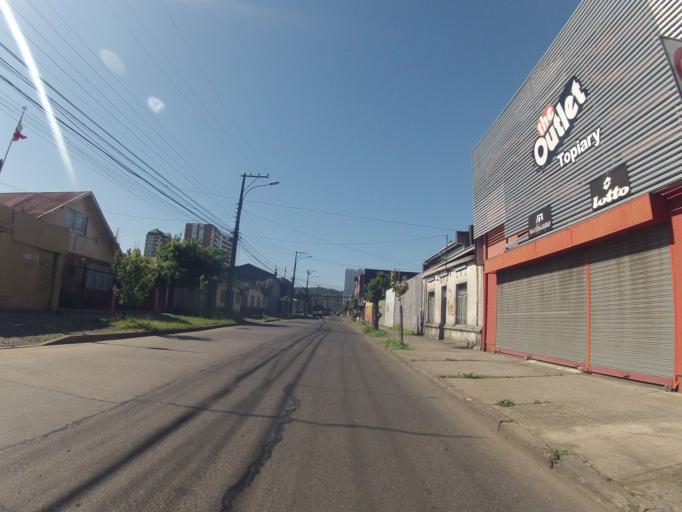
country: CL
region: Araucania
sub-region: Provincia de Cautin
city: Temuco
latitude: -38.7430
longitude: -72.5943
